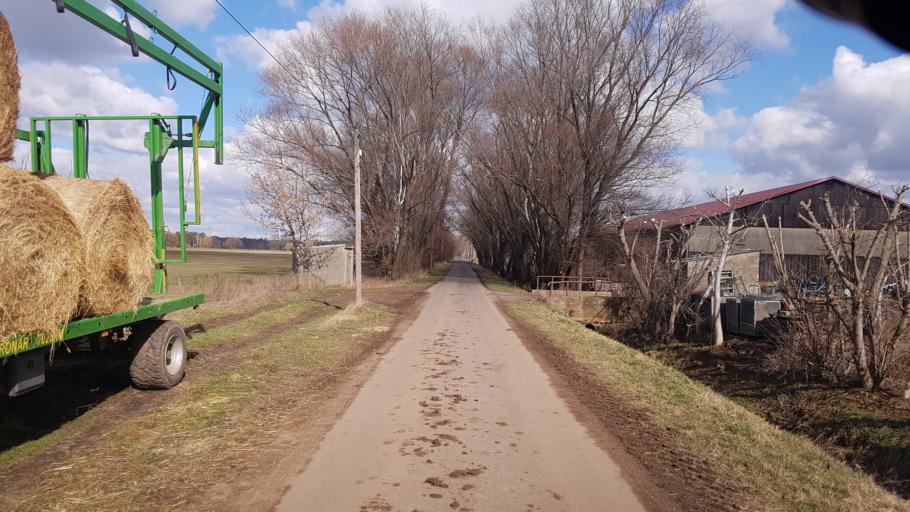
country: DE
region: Brandenburg
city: Falkenberg
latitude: 51.5936
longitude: 13.2158
